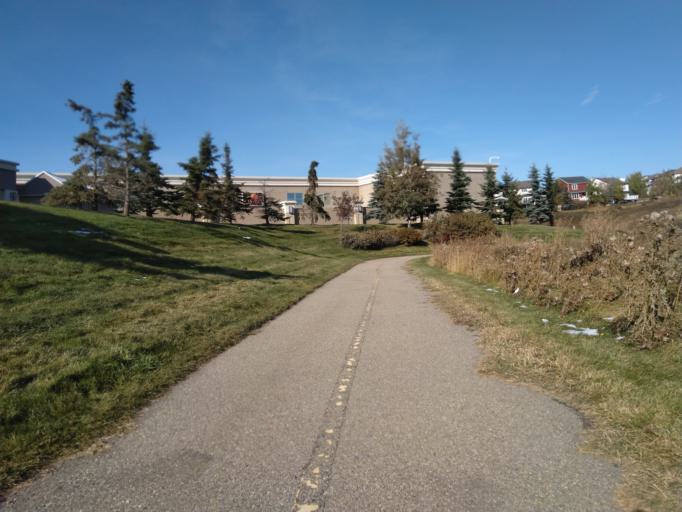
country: CA
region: Alberta
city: Calgary
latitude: 51.1608
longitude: -114.1219
